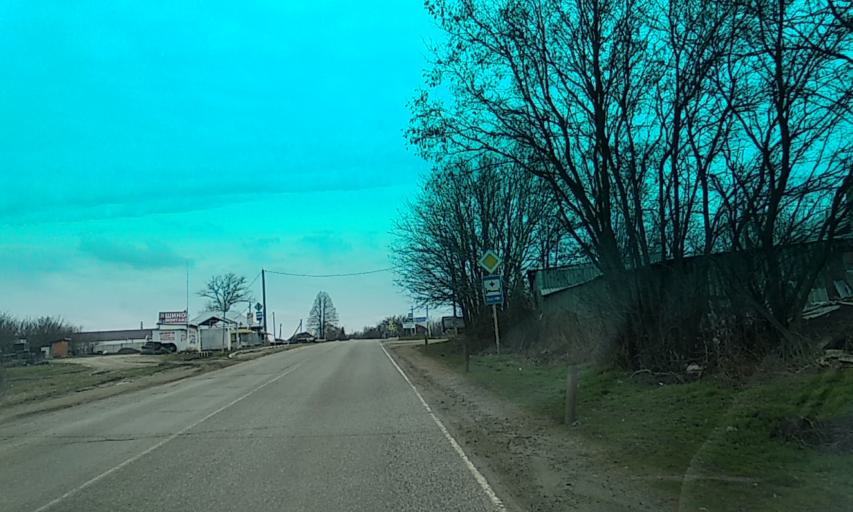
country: RU
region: Krasnodarskiy
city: Dvubratskiy
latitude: 45.3771
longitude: 39.7132
